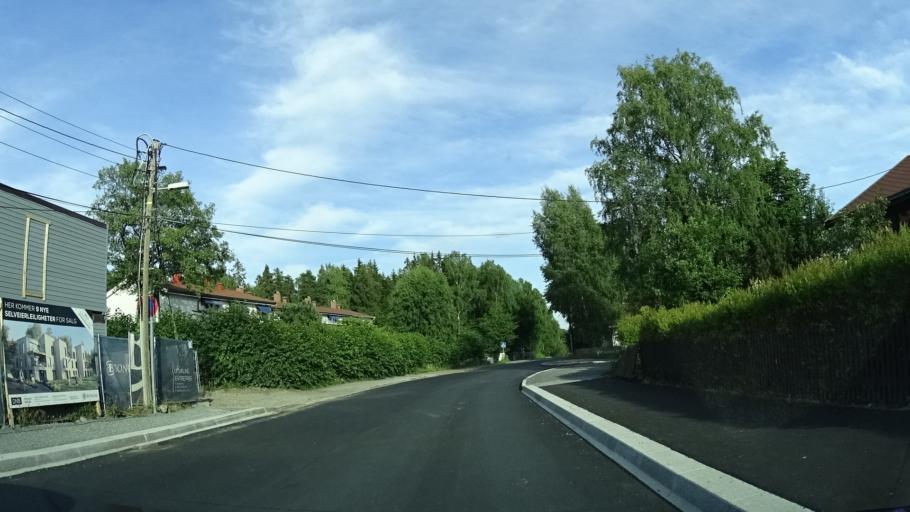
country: NO
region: Oslo
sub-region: Oslo
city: Sjolyststranda
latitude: 59.9526
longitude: 10.6605
